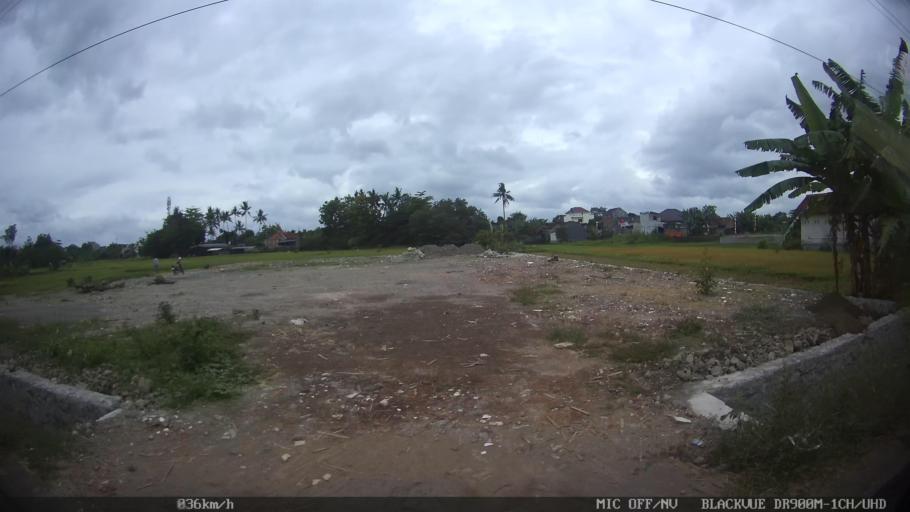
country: ID
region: Daerah Istimewa Yogyakarta
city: Sewon
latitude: -7.8489
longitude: 110.4135
